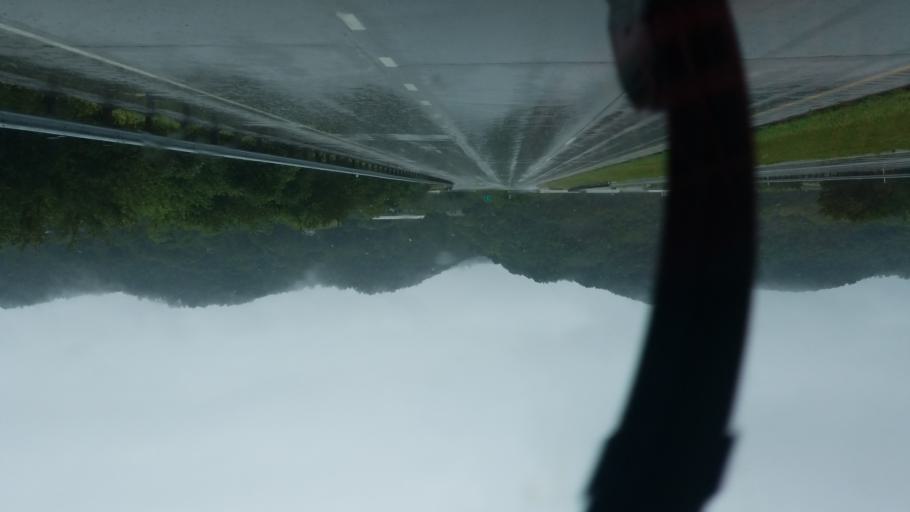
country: US
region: Ohio
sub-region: Scioto County
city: West Portsmouth
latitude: 38.7370
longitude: -83.0300
